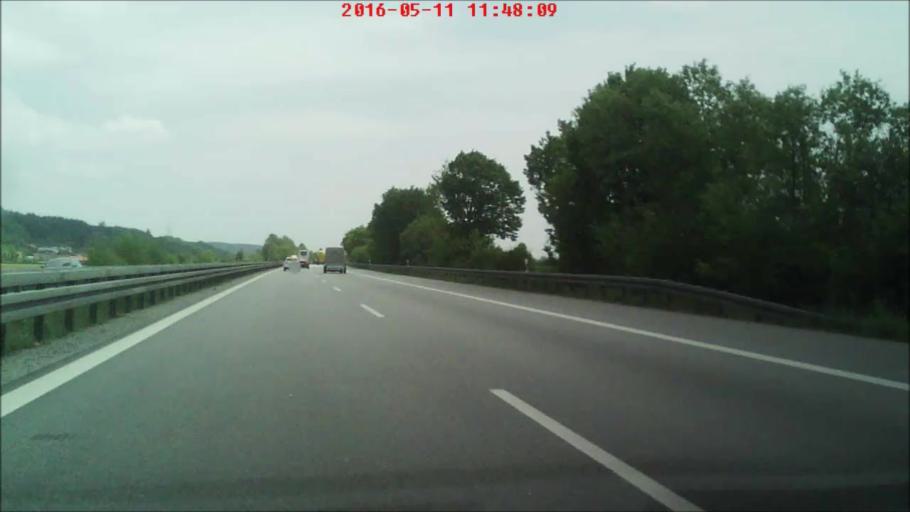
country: DE
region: Bavaria
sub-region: Upper Palatinate
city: Worth an der Donau
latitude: 48.9897
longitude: 12.4367
